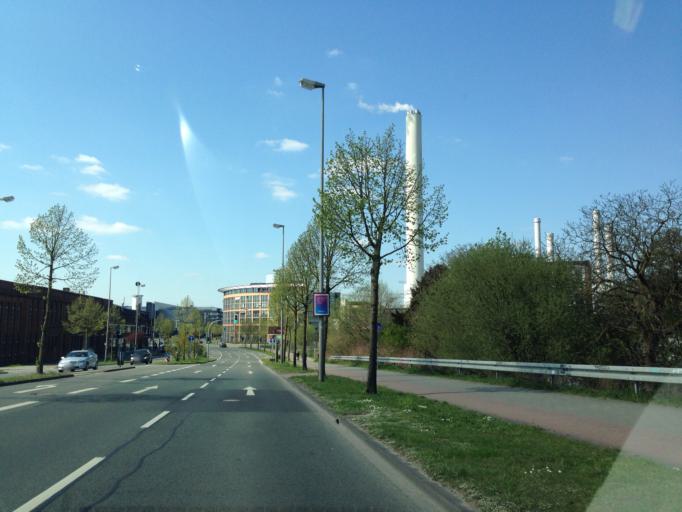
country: DE
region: North Rhine-Westphalia
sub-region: Regierungsbezirk Munster
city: Muenster
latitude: 51.9474
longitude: 7.6428
